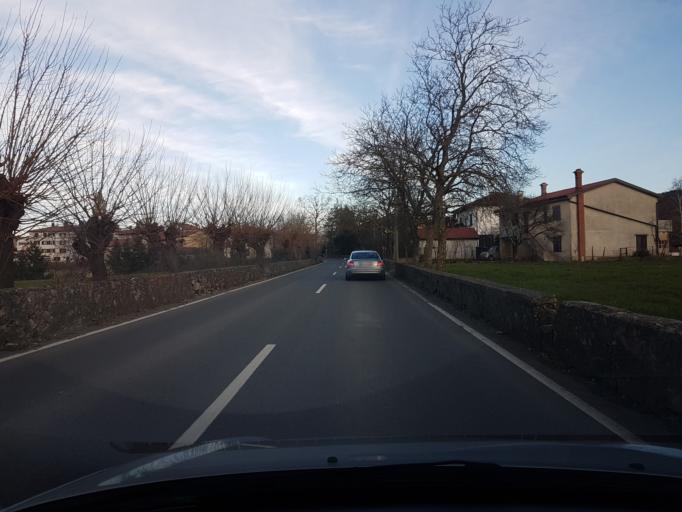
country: SI
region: Divaca
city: Divaca
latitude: 45.6610
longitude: 13.9244
